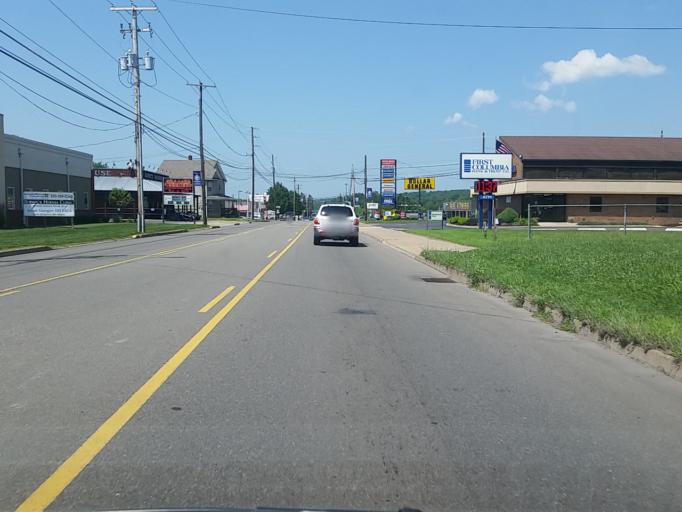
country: US
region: Pennsylvania
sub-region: Columbia County
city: Berwick
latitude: 41.0475
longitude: -76.2697
